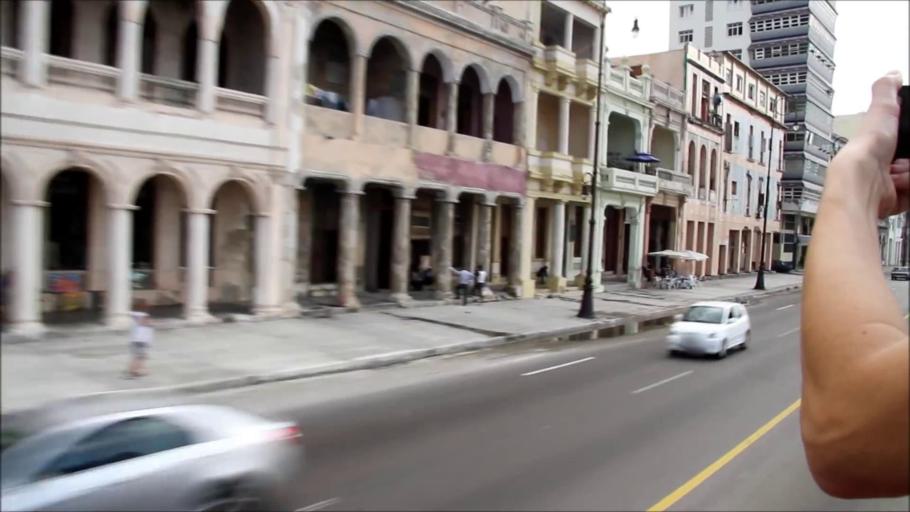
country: CU
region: La Habana
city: Centro Habana
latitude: 23.1447
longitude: -82.3605
